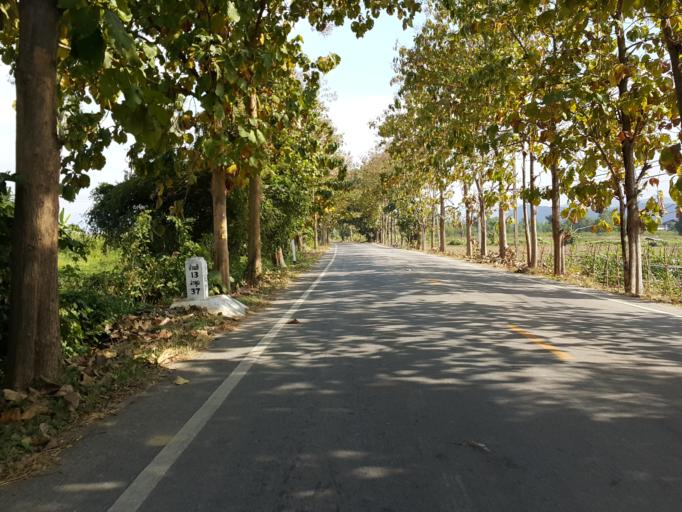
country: TH
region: Chiang Mai
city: San Kamphaeng
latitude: 18.7254
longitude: 99.1583
